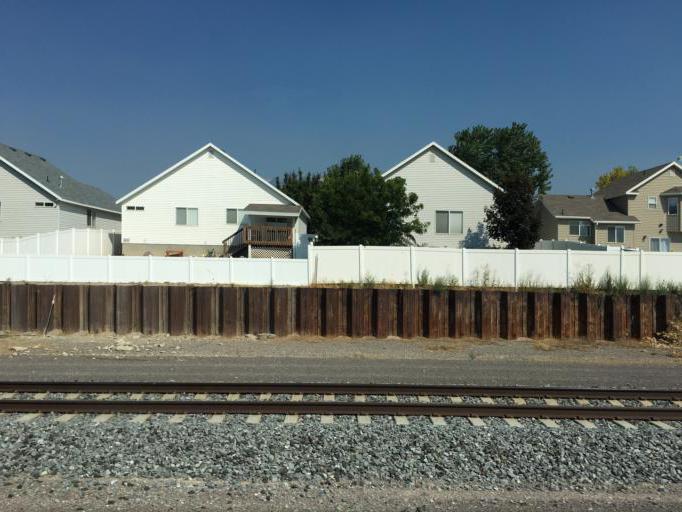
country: US
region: Utah
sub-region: Salt Lake County
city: South Jordan
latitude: 40.5397
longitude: -111.9036
